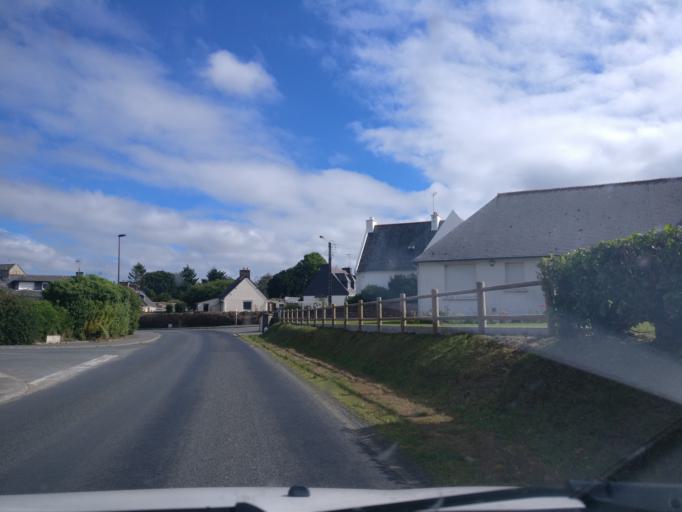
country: FR
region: Brittany
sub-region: Departement des Cotes-d'Armor
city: Rospez
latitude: 48.7276
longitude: -3.3864
